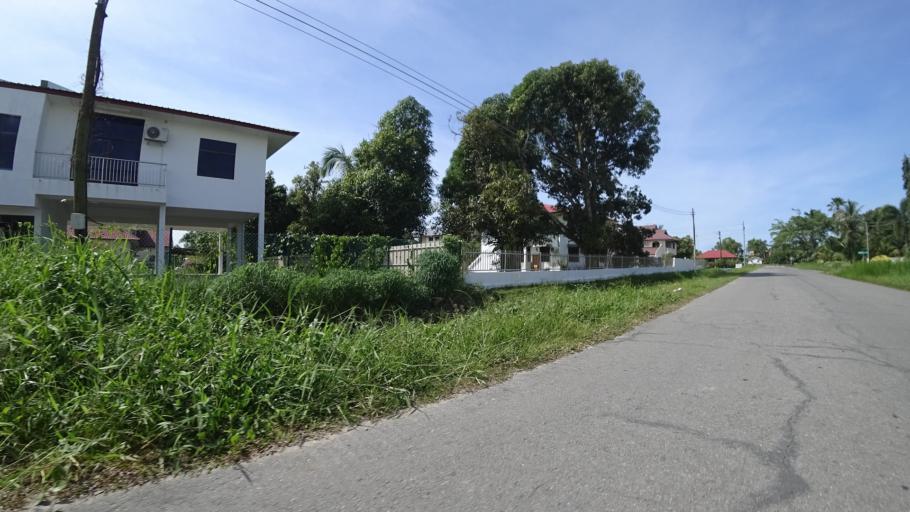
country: BN
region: Brunei and Muara
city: Bandar Seri Begawan
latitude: 4.8826
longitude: 114.8491
